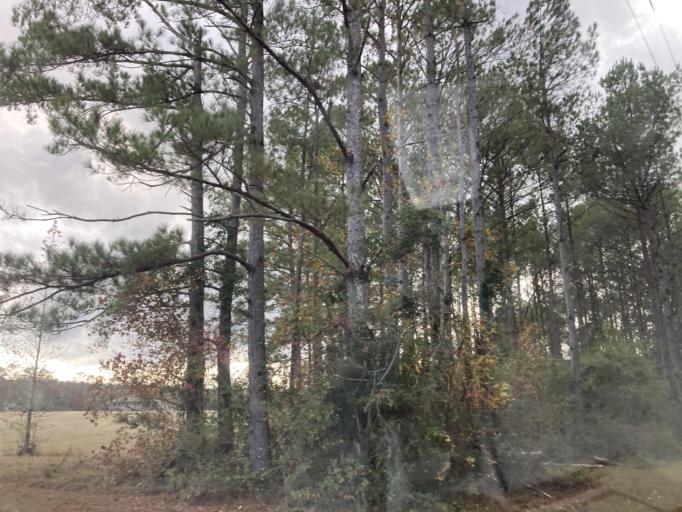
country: US
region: Mississippi
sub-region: Lamar County
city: Purvis
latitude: 31.1602
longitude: -89.6166
